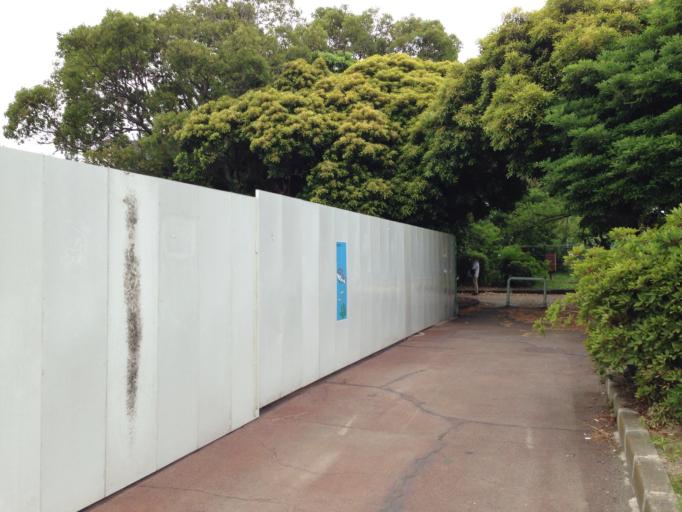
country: JP
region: Tokyo
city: Tokyo
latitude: 35.6487
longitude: 139.7703
